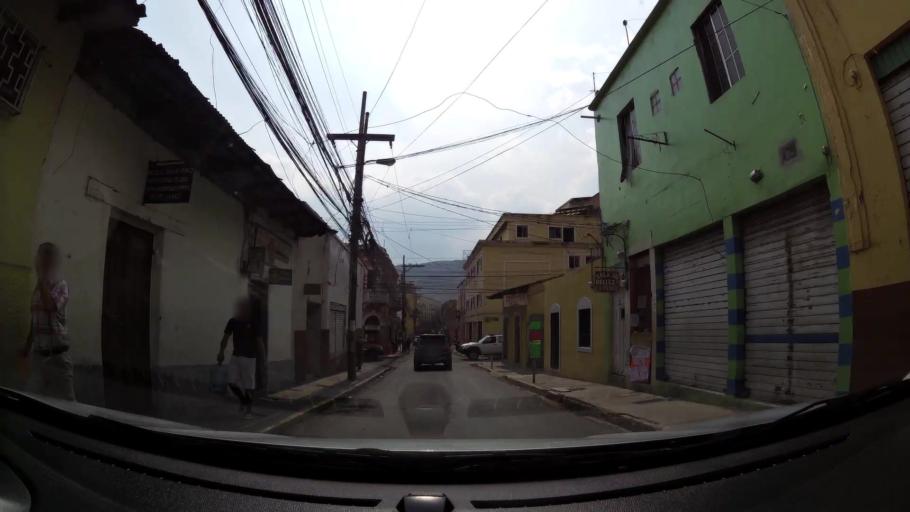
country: HN
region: Francisco Morazan
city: Tegucigalpa
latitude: 14.1069
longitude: -87.2034
